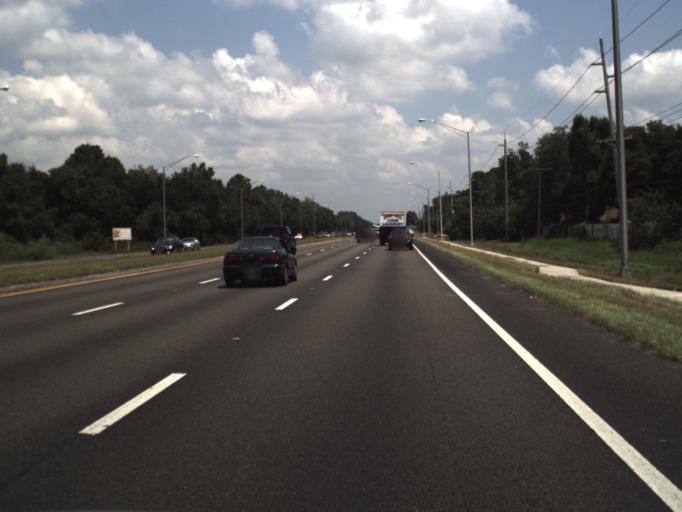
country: US
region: Florida
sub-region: Hillsborough County
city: Greater Northdale
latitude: 28.1143
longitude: -82.5024
